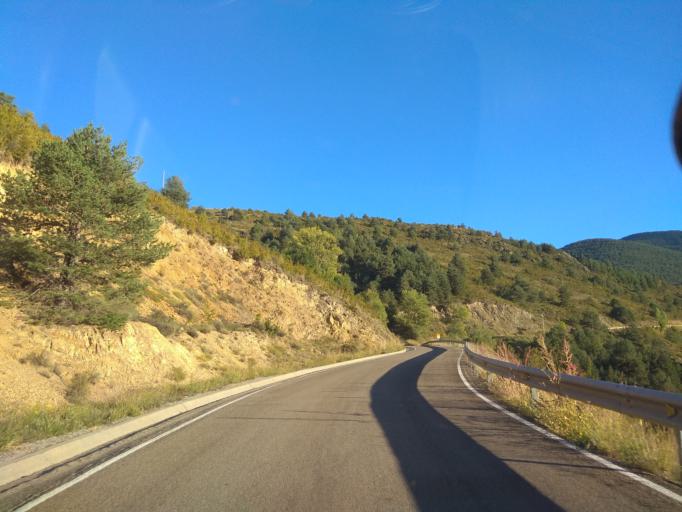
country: ES
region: Catalonia
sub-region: Provincia de Lleida
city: Lles de Cerdanya
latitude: 42.3554
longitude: 1.6887
